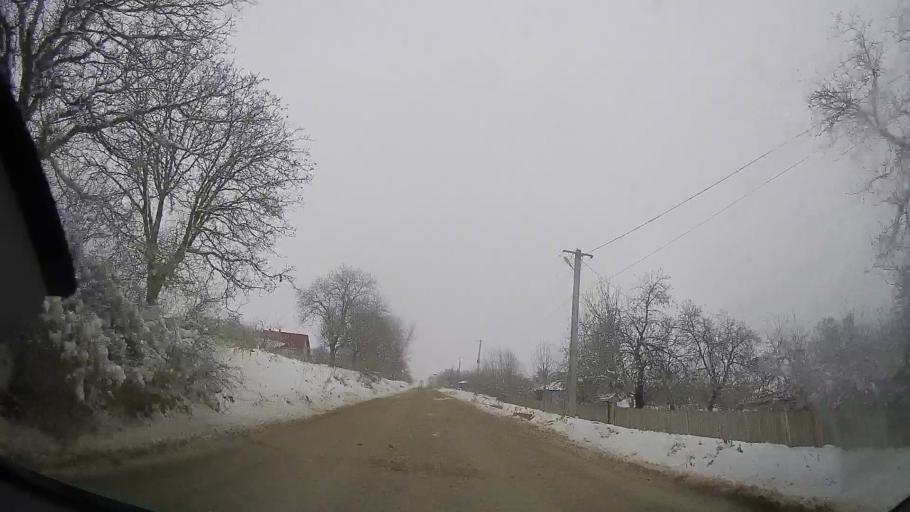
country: RO
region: Vaslui
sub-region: Comuna Todiresti
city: Todiresti
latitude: 46.8754
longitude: 27.3770
